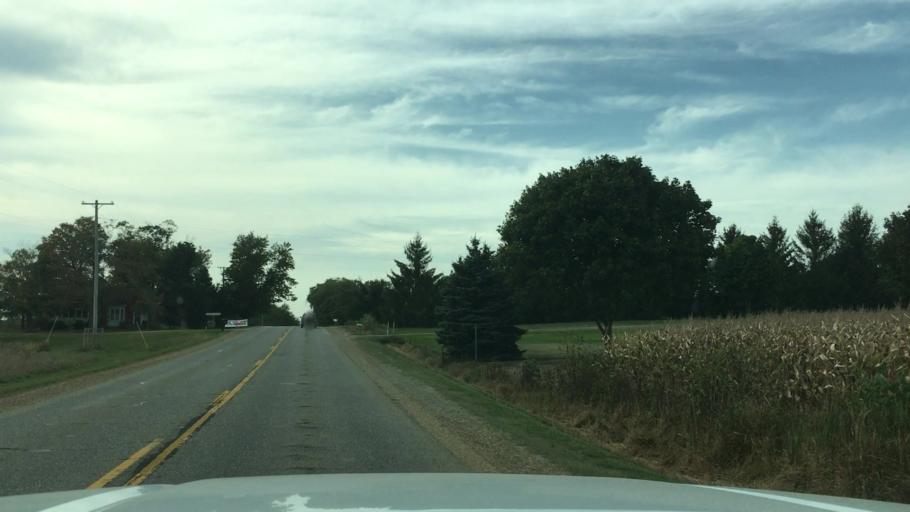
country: US
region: Michigan
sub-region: Ottawa County
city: Hudsonville
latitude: 42.7821
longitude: -85.8677
